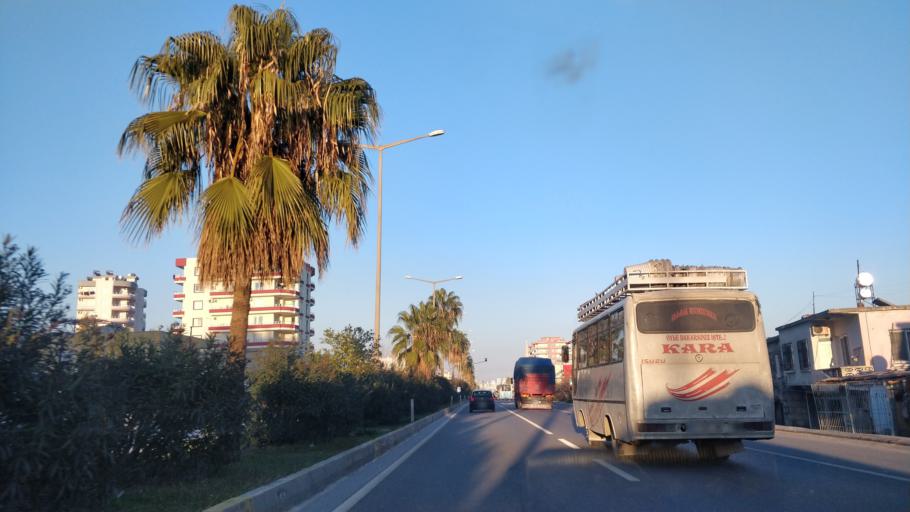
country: TR
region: Mersin
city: Tomuk
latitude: 36.6852
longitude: 34.4220
